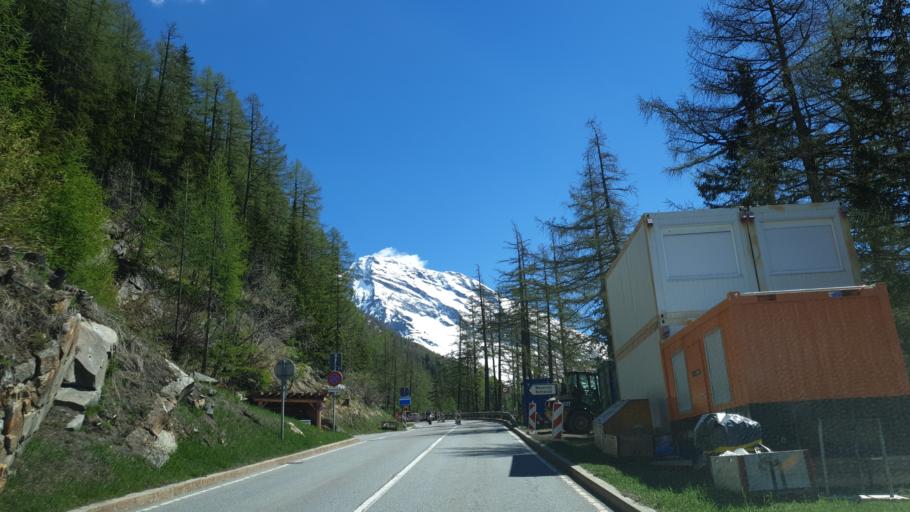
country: CH
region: Valais
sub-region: Brig District
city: Brig
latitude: 46.2789
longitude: 8.0381
